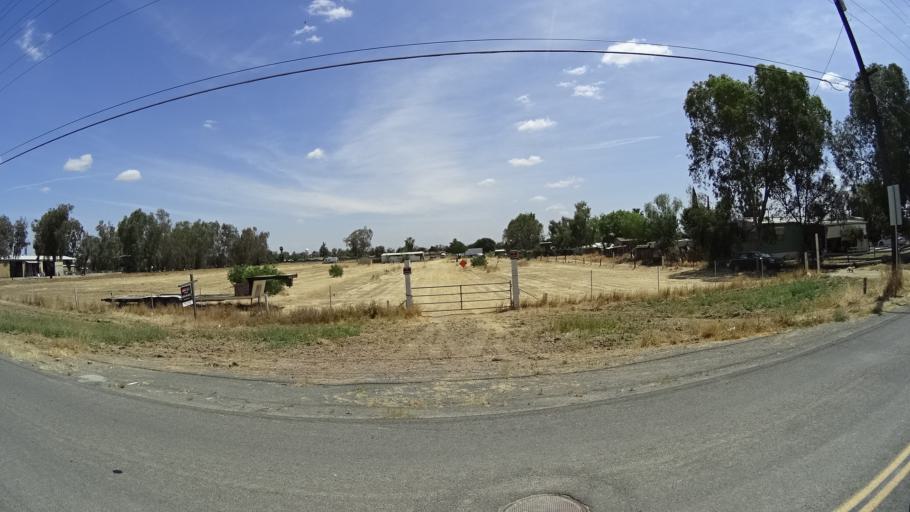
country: US
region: California
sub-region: Kings County
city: Home Garden
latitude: 36.3105
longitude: -119.6461
